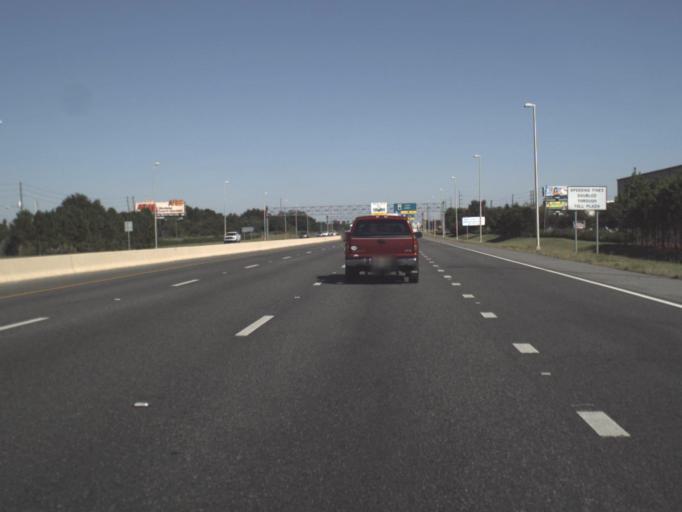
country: US
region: Florida
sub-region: Orange County
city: Sky Lake
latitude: 28.4418
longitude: -81.3929
